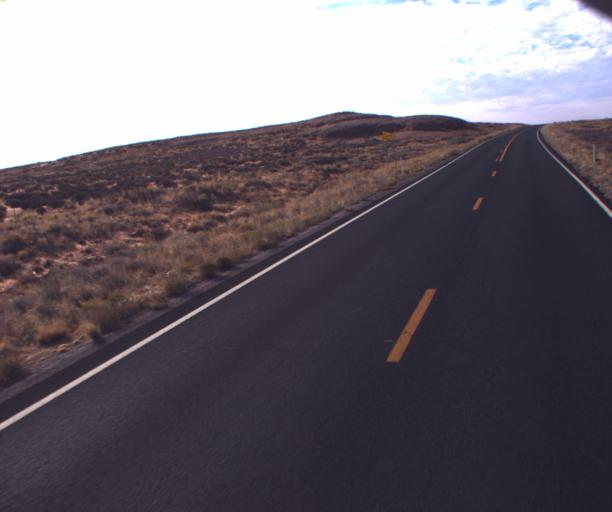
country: US
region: Arizona
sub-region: Apache County
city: Many Farms
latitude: 36.8867
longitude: -109.6277
